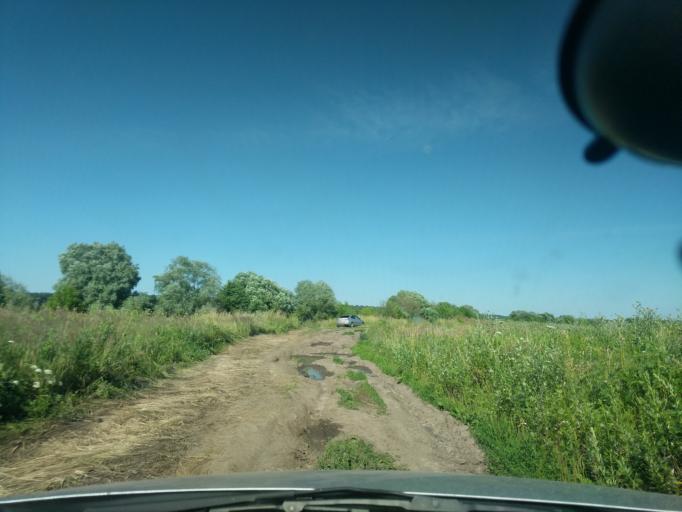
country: RU
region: Moskovskaya
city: Pushchino
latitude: 54.8484
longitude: 37.6455
